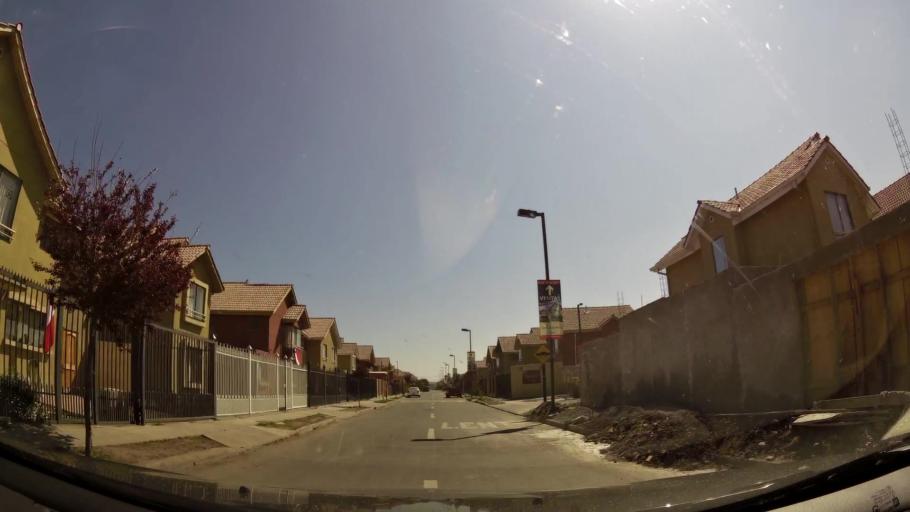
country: CL
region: Santiago Metropolitan
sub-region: Provincia de Chacabuco
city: Chicureo Abajo
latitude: -33.3260
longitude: -70.7527
